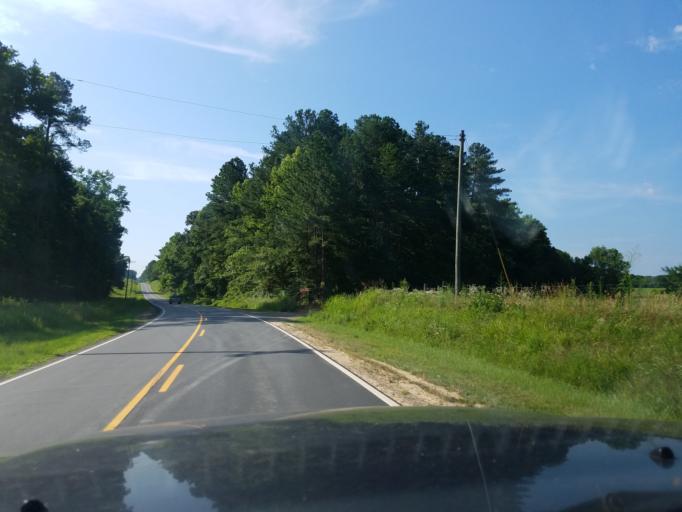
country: US
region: North Carolina
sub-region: Granville County
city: Butner
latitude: 36.1732
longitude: -78.7935
